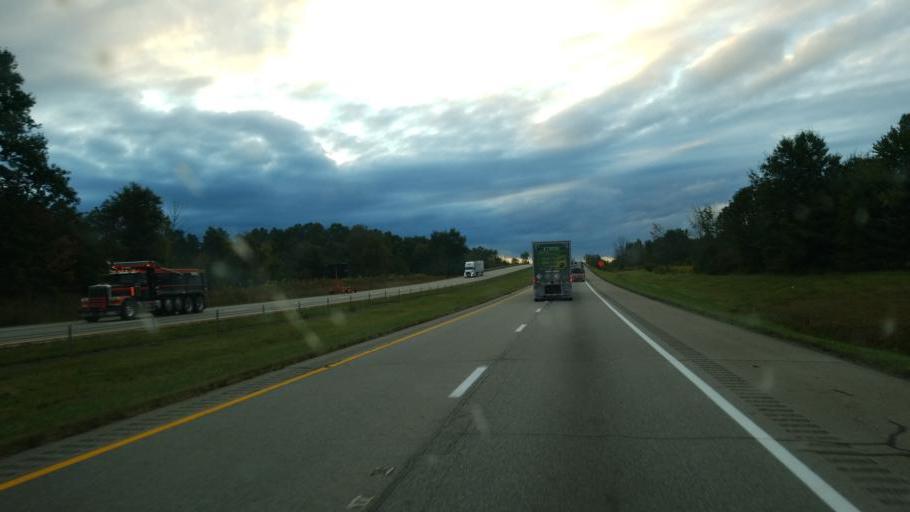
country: US
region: Ohio
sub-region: Mahoning County
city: Craig Beach
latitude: 41.1030
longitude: -81.0291
